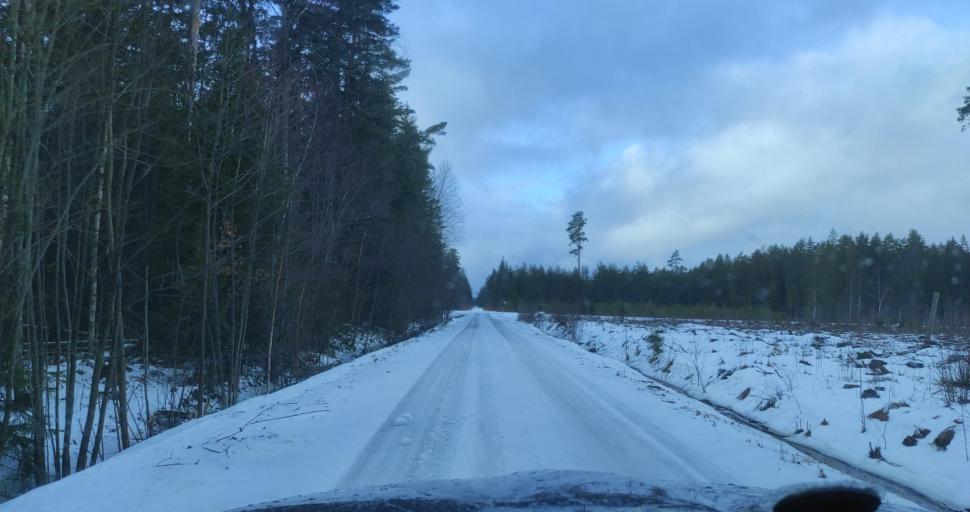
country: LV
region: Dundaga
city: Dundaga
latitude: 57.4112
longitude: 22.0811
